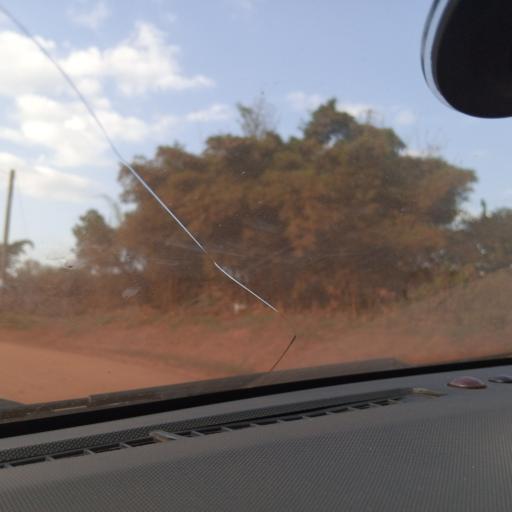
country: UG
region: Central Region
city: Masaka
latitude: -0.3563
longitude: 31.7426
